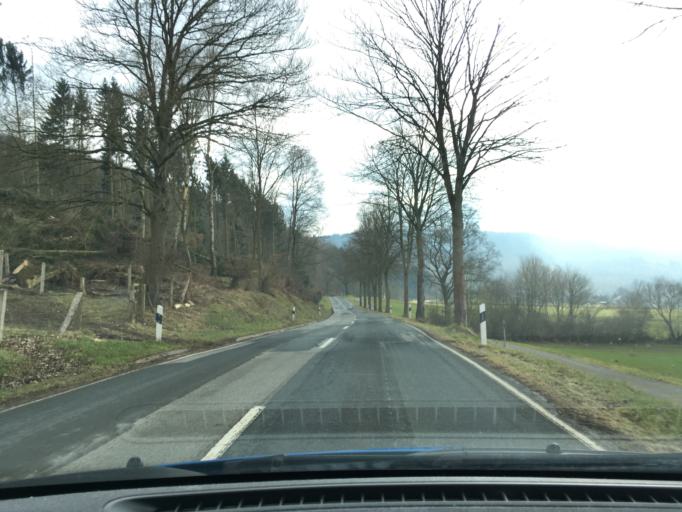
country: DE
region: Lower Saxony
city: Buhren
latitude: 51.5337
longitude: 9.6238
